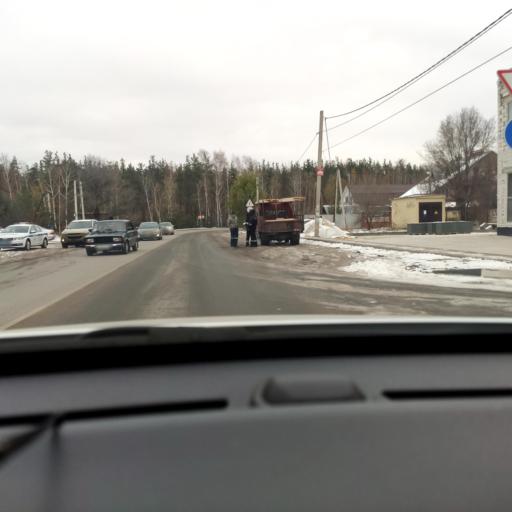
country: RU
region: Voronezj
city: Somovo
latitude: 51.7392
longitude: 39.2923
